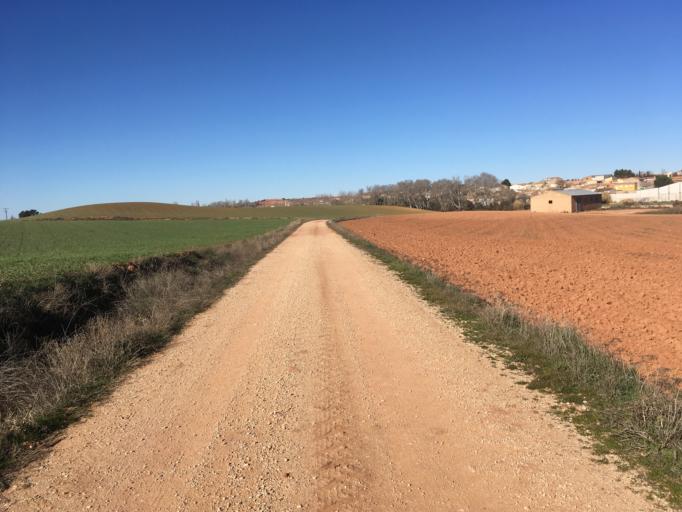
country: ES
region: Castille-La Mancha
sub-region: Provincia de Cuenca
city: Atalaya del Canavate
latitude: 39.5439
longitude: -2.2457
